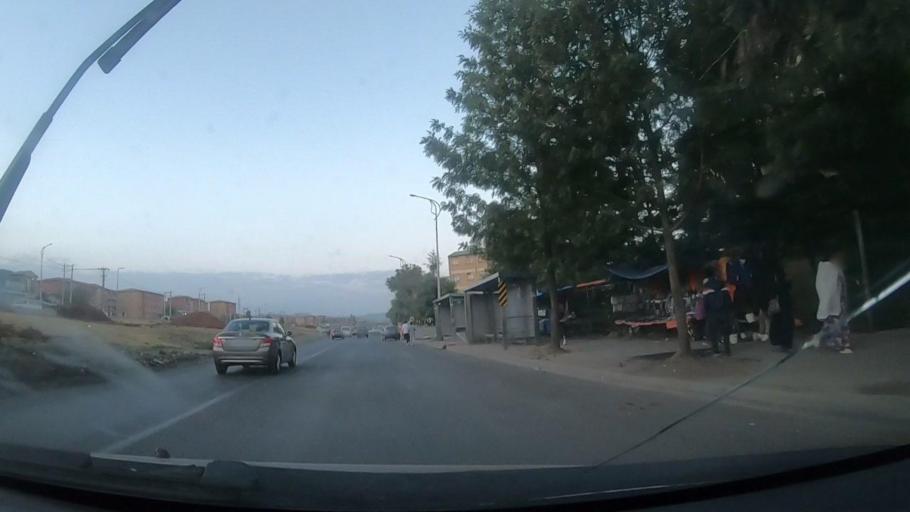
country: ET
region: Adis Abeba
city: Addis Ababa
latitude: 9.0378
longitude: 38.8778
